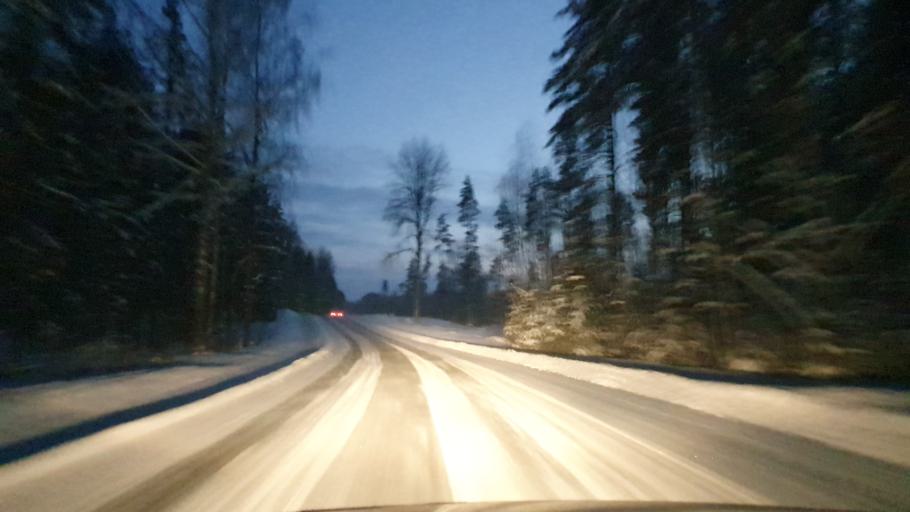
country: EE
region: Vorumaa
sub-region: Antsla vald
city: Vana-Antsla
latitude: 57.9751
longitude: 26.7605
